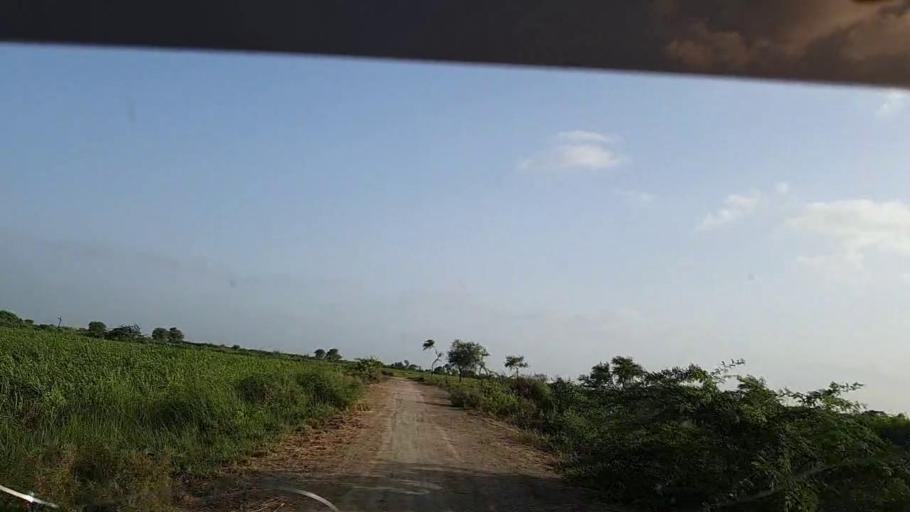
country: PK
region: Sindh
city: Badin
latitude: 24.5525
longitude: 68.8636
